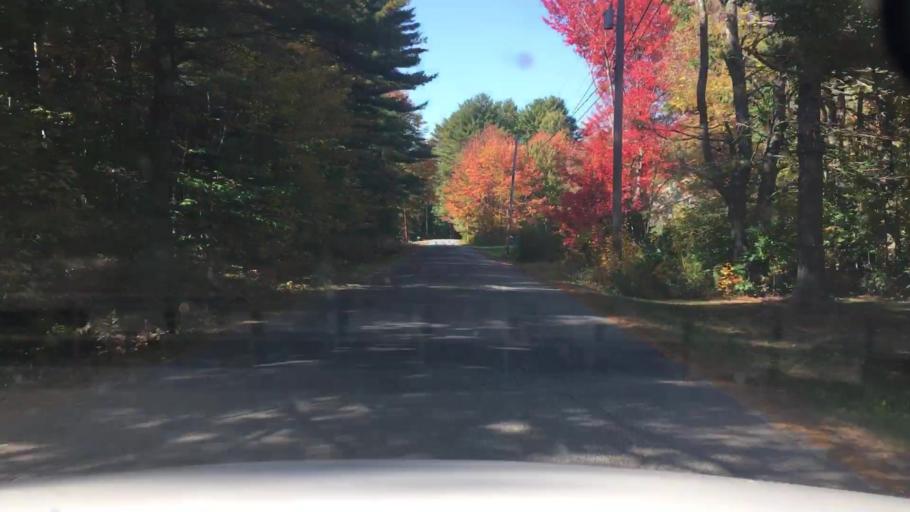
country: US
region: Maine
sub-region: Androscoggin County
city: Lisbon Falls
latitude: 44.0172
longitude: -69.9825
